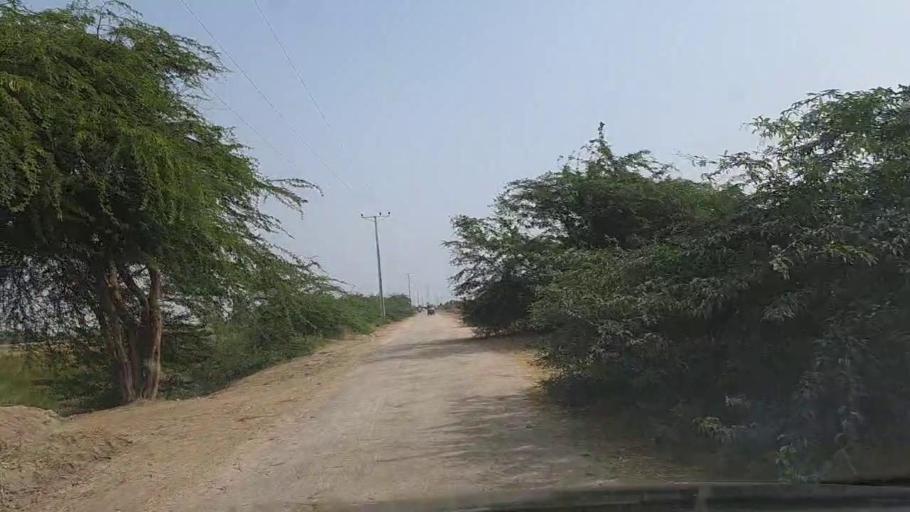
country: PK
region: Sindh
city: Thatta
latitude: 24.7855
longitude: 67.8590
